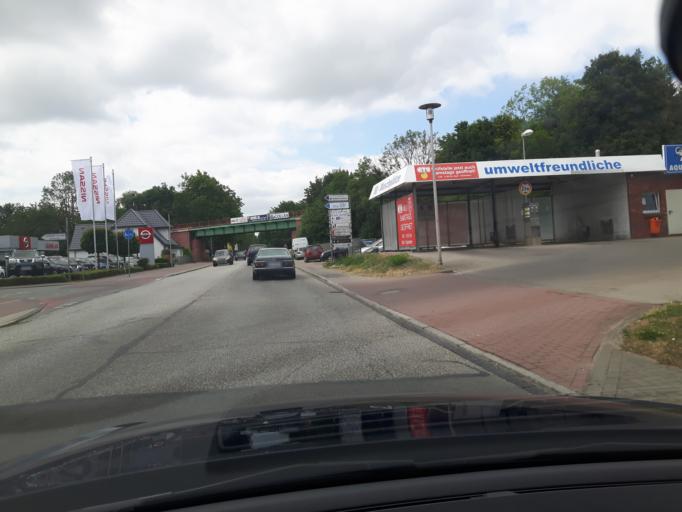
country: DE
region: Schleswig-Holstein
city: Neustadt in Holstein
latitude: 54.1026
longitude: 10.7997
